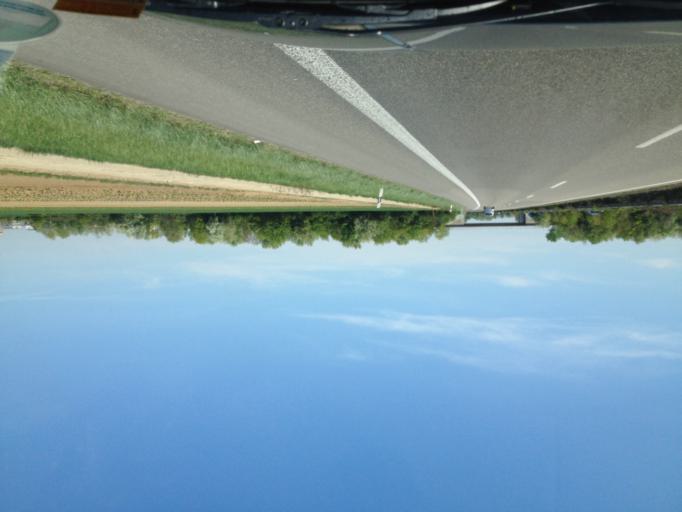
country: DE
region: Rheinland-Pfalz
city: Limburgerhof
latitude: 49.4410
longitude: 8.3781
